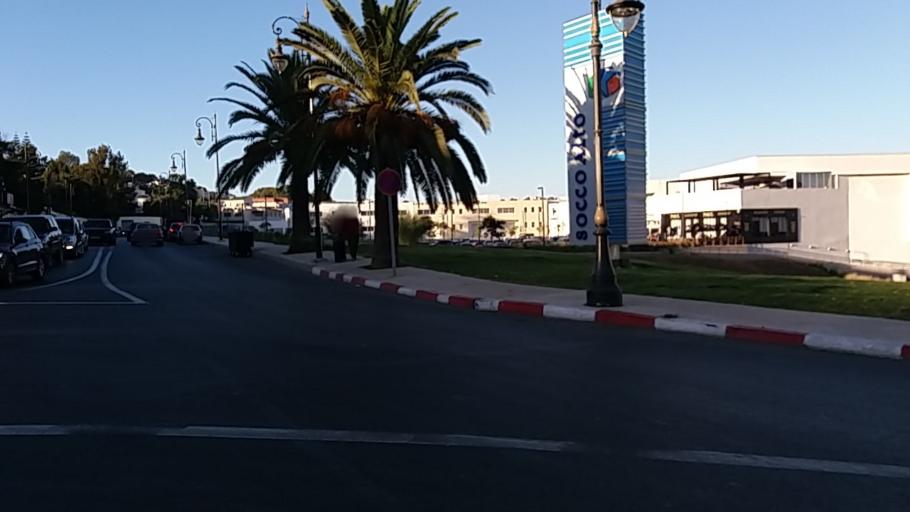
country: MA
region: Tanger-Tetouan
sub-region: Tanger-Assilah
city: Tangier
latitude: 35.7811
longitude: -5.8424
